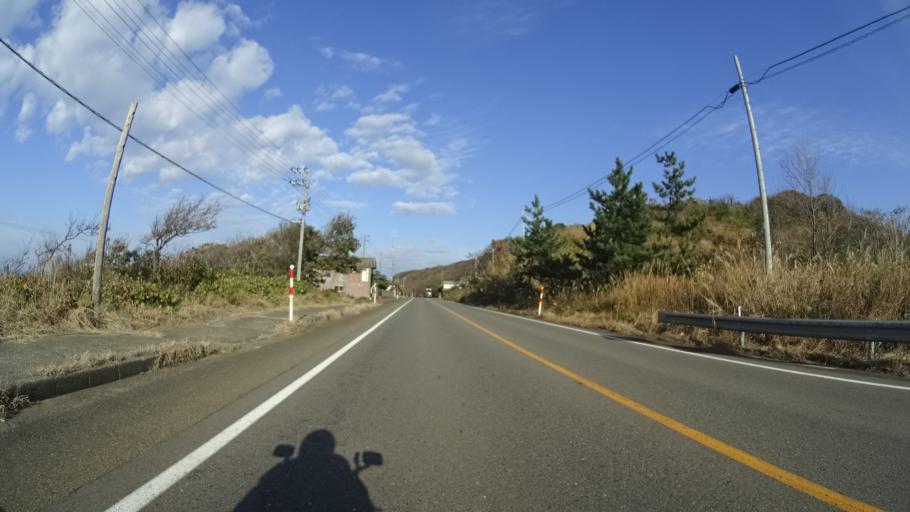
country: JP
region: Niigata
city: Kashiwazaki
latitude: 37.2924
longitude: 138.4030
